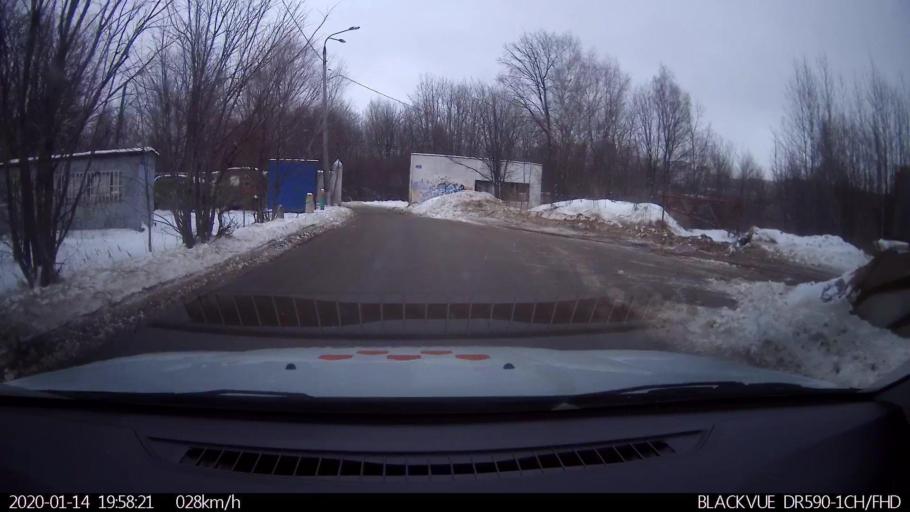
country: RU
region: Nizjnij Novgorod
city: Nizhniy Novgorod
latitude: 56.2371
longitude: 43.9396
